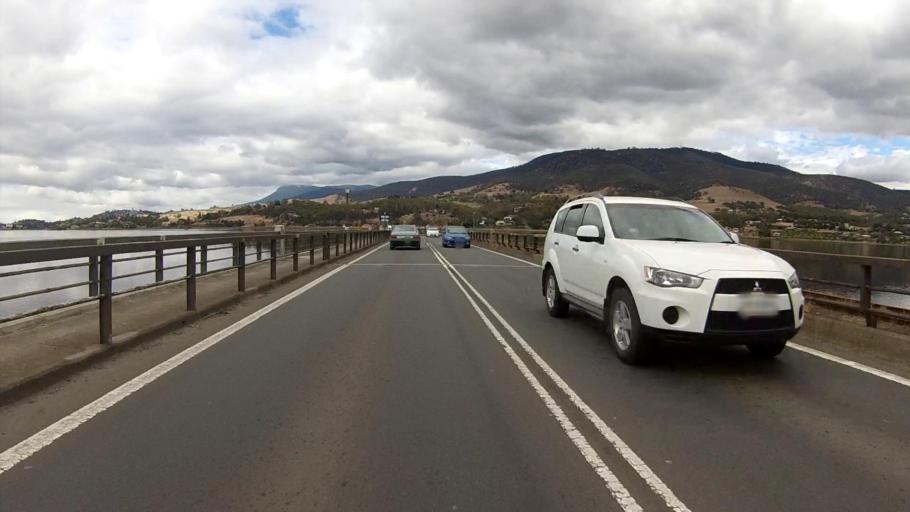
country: AU
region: Tasmania
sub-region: Brighton
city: Bridgewater
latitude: -42.7418
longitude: 147.2254
